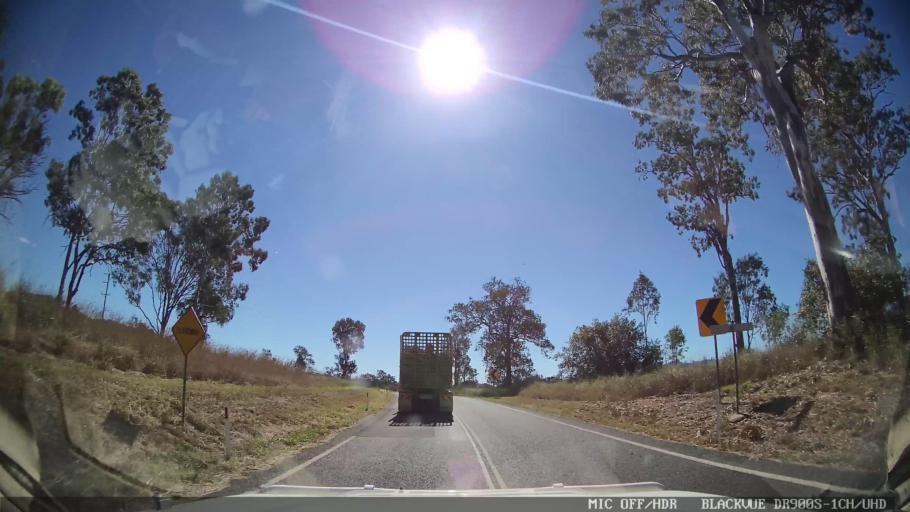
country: AU
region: Queensland
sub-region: Gladstone
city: Toolooa
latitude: -24.2733
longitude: 151.2760
